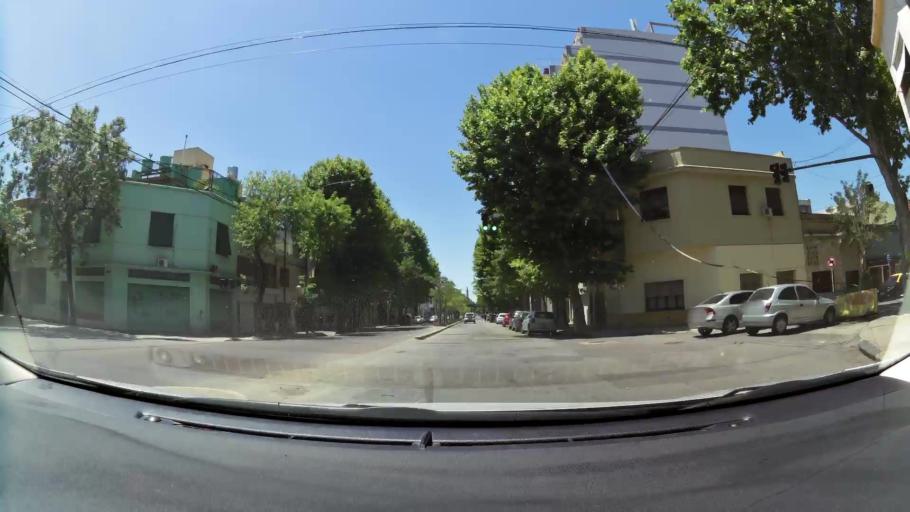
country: AR
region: Buenos Aires
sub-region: Partido de Avellaneda
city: Avellaneda
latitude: -34.6500
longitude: -58.3826
